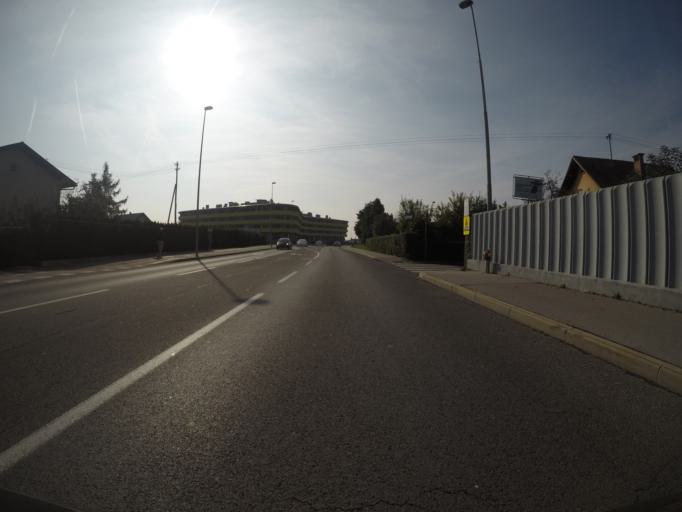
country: SI
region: Kamnik
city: Smarca
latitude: 46.2094
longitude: 14.5987
